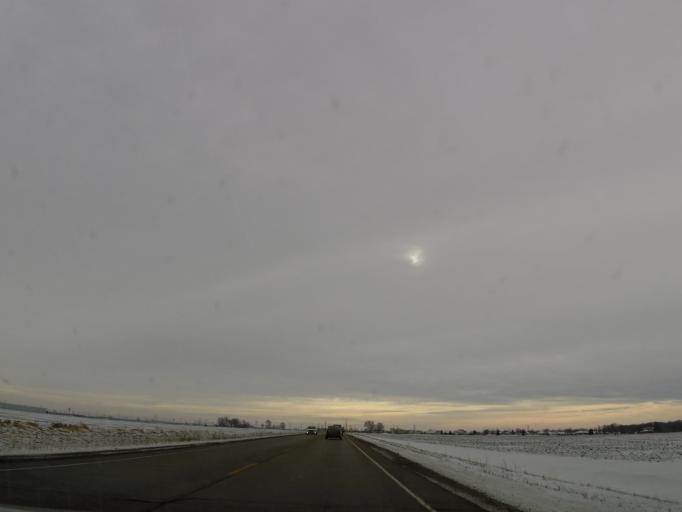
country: US
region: Illinois
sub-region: LaSalle County
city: Peru
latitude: 41.3006
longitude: -89.1063
